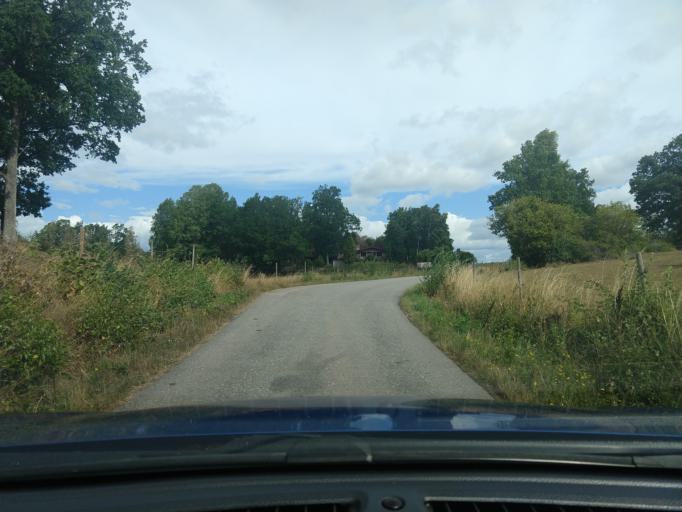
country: SE
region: Blekinge
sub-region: Ronneby Kommun
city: Brakne-Hoby
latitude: 56.2927
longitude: 15.1951
